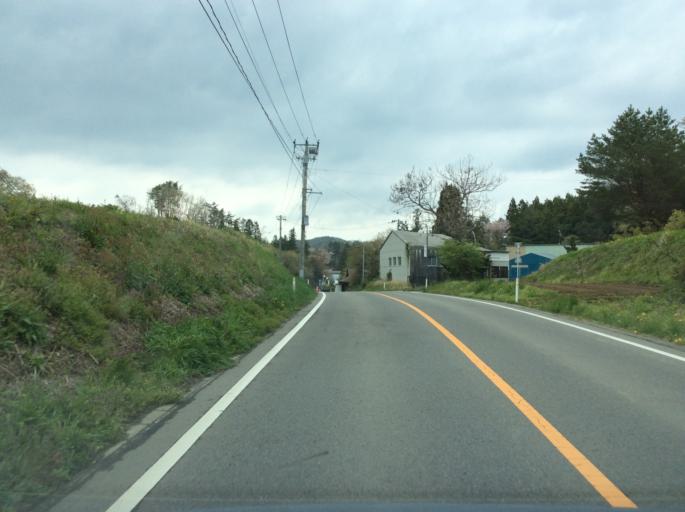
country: JP
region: Fukushima
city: Funehikimachi-funehiki
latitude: 37.3849
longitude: 140.5890
